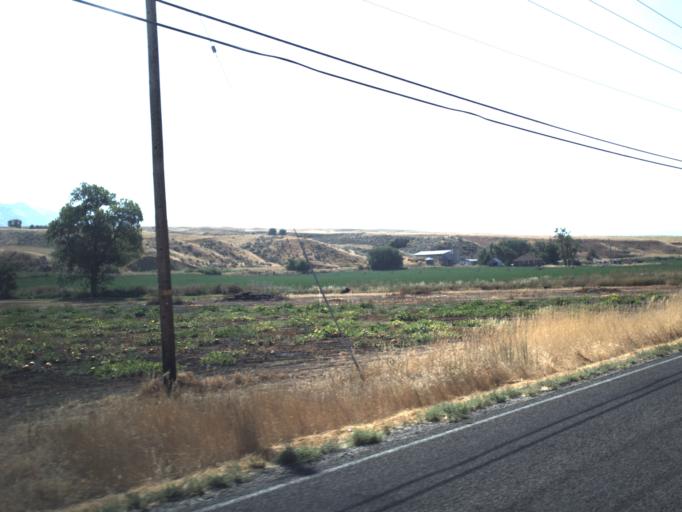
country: US
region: Utah
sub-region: Cache County
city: Hyrum
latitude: 41.6043
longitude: -111.8332
